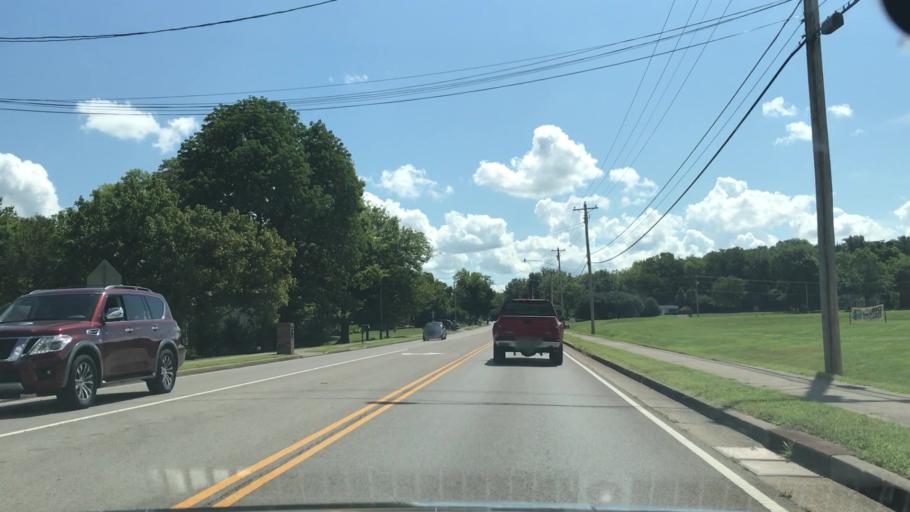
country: US
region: Tennessee
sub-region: Williamson County
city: Franklin
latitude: 35.9291
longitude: -86.8515
